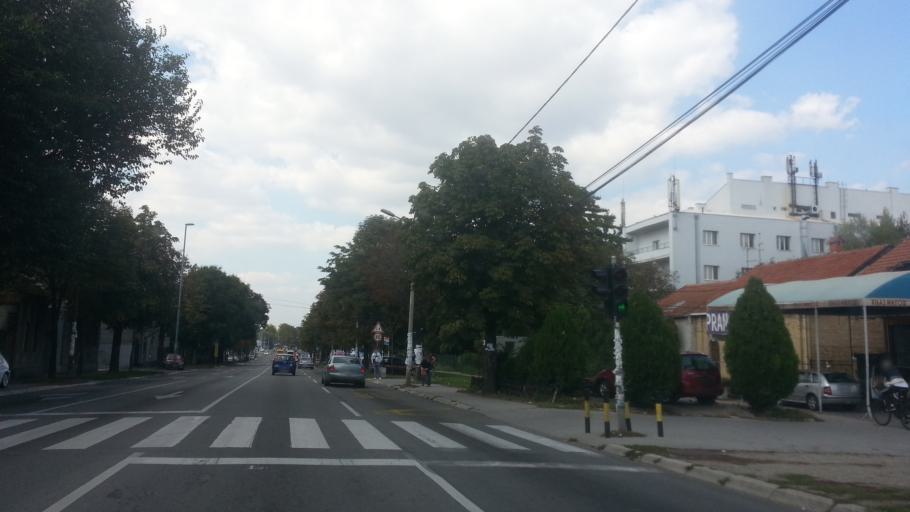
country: RS
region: Central Serbia
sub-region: Belgrade
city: Zemun
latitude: 44.8575
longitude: 20.3814
